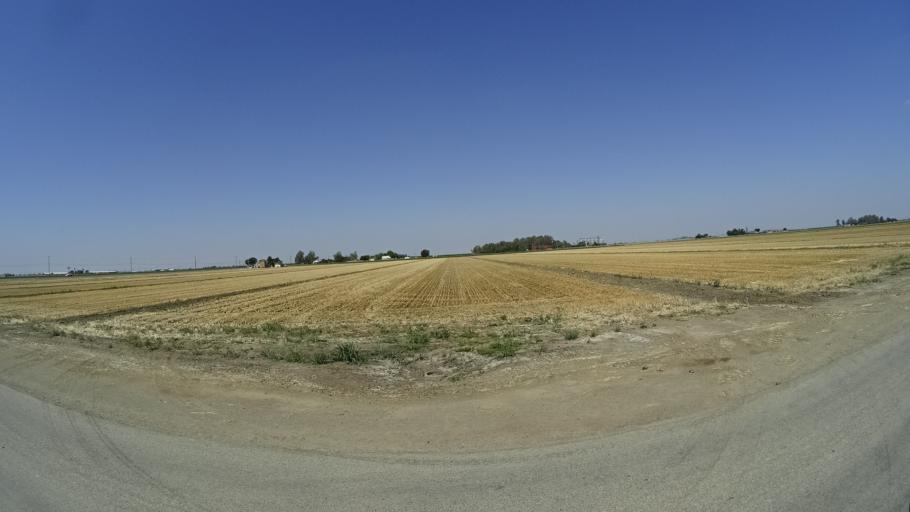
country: US
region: California
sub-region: Kings County
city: Home Garden
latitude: 36.2129
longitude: -119.6279
